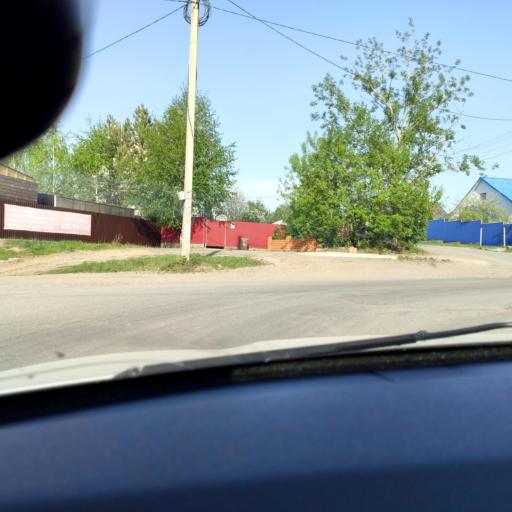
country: RU
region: Perm
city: Polazna
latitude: 58.2984
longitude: 56.3951
